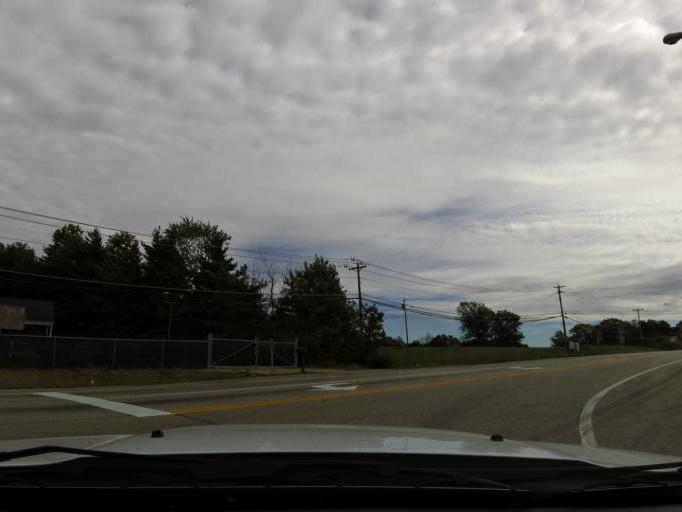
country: US
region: Ohio
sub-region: Hamilton County
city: Delhi Hills
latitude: 39.0737
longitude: -84.6534
